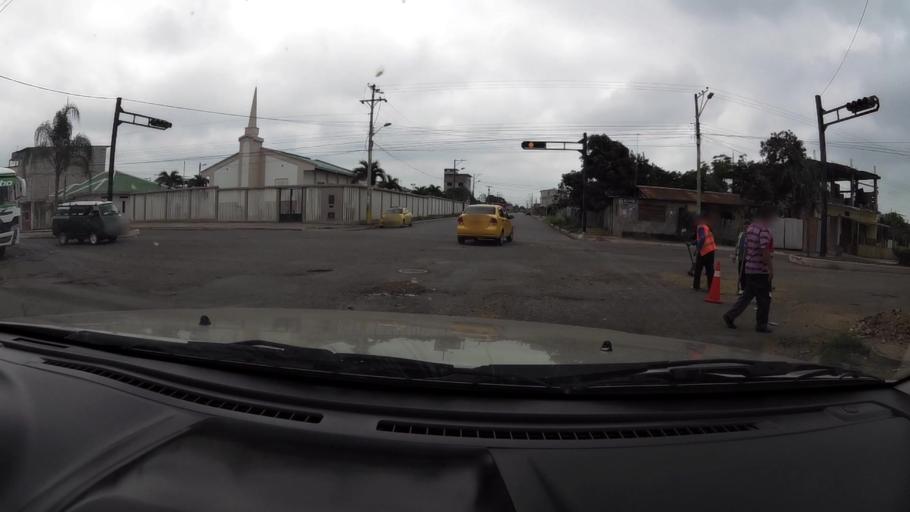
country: EC
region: El Oro
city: Pasaje
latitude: -3.2418
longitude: -79.8338
